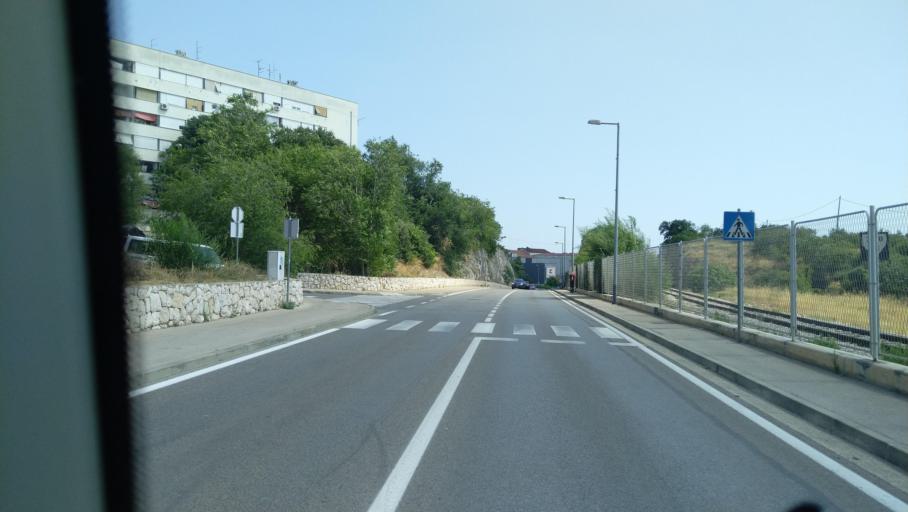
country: HR
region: Sibensko-Kniniska
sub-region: Grad Sibenik
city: Sibenik
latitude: 43.7265
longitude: 15.9036
